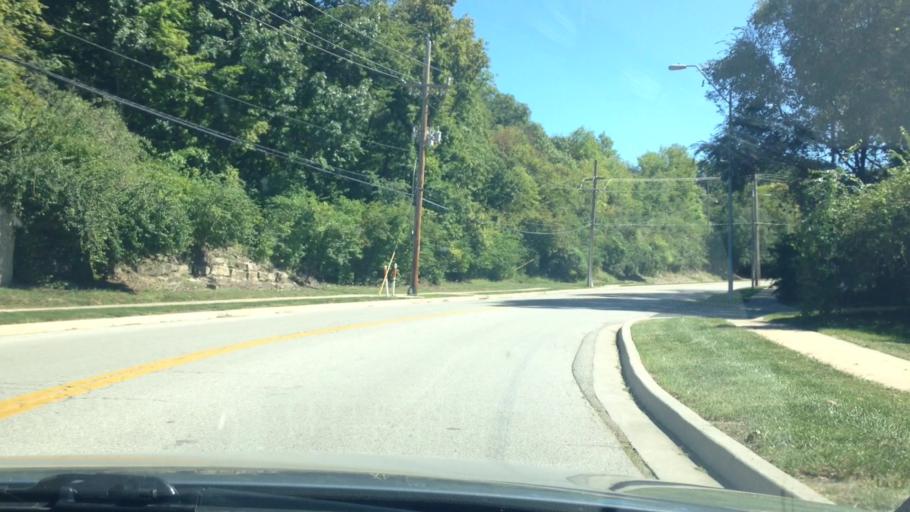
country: US
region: Missouri
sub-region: Jackson County
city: Raytown
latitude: 39.0117
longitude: -94.5058
